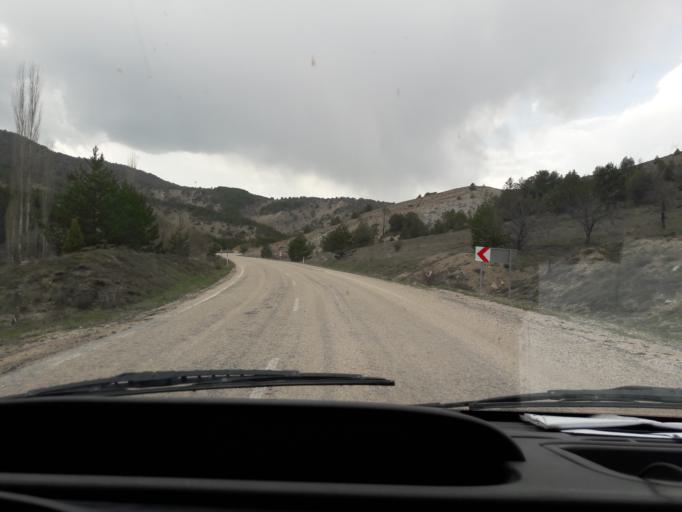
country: TR
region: Giresun
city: Alucra
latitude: 40.2766
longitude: 38.8266
